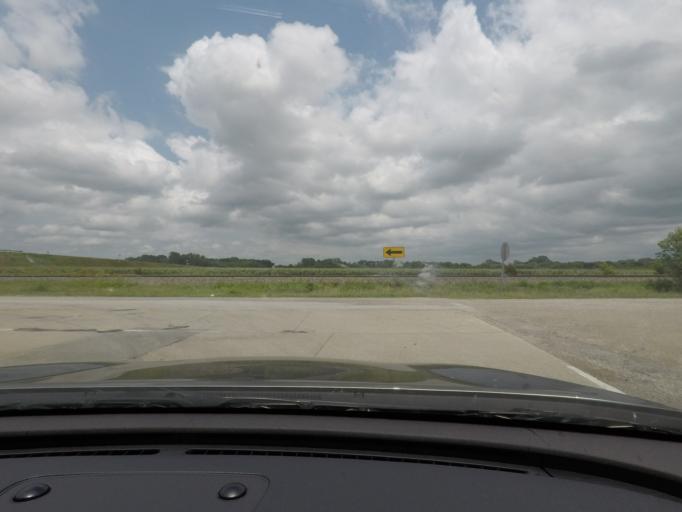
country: US
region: Missouri
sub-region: Carroll County
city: Carrollton
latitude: 39.3376
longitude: -93.4893
